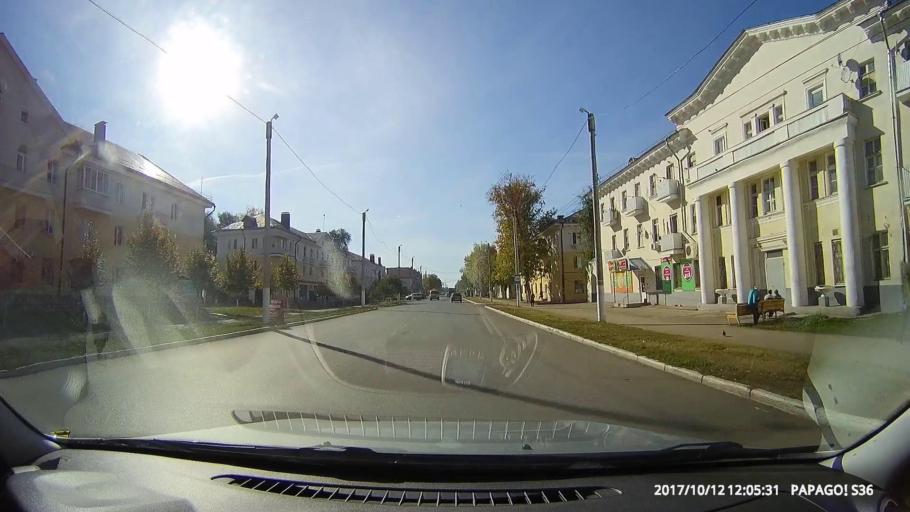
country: RU
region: Samara
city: Chapayevsk
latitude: 52.9767
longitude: 49.7116
